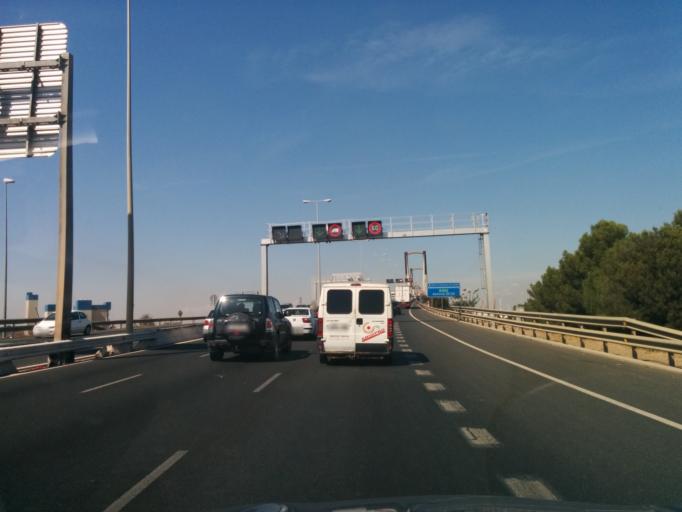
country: ES
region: Andalusia
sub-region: Provincia de Sevilla
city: Gelves
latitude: 37.3426
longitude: -5.9857
